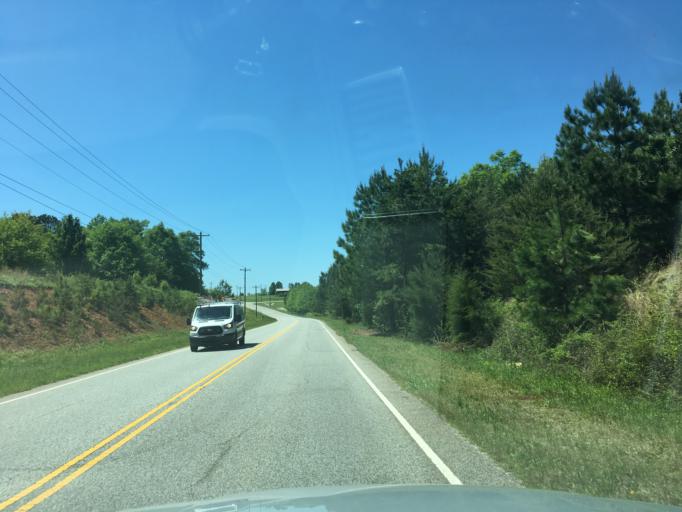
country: US
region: South Carolina
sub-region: Greenville County
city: Greer
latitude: 34.8835
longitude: -82.1877
